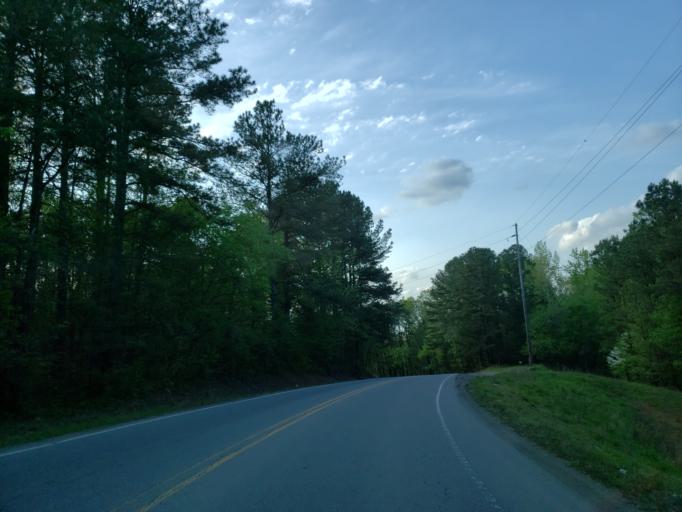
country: US
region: Georgia
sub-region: Cherokee County
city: Ball Ground
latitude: 34.2925
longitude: -84.3909
